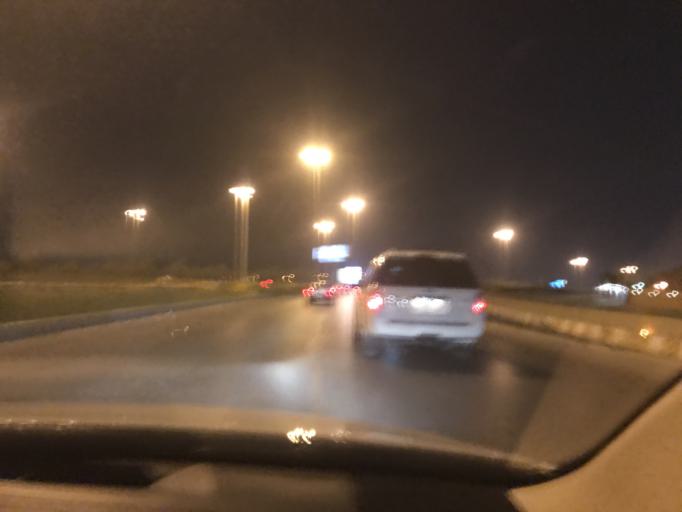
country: SA
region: Ar Riyad
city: Riyadh
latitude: 24.7915
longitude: 46.7246
